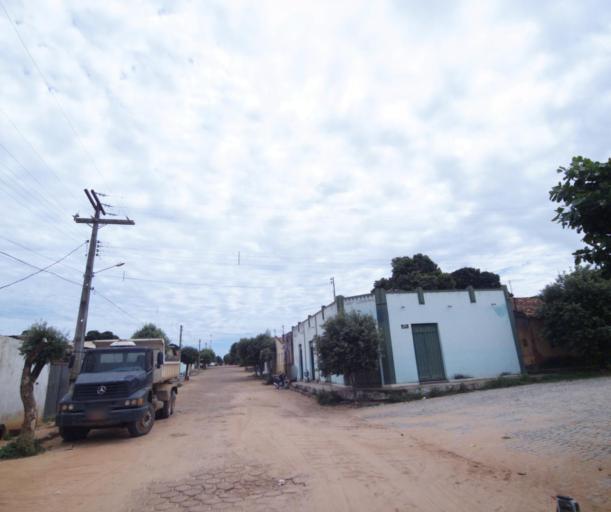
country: BR
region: Bahia
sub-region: Carinhanha
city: Carinhanha
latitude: -14.2134
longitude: -44.2834
